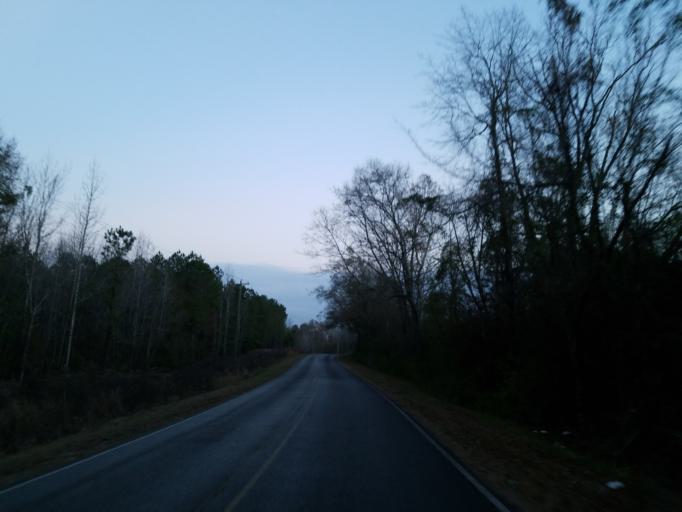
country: US
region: Alabama
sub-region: Sumter County
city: York
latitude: 32.4026
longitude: -88.4625
